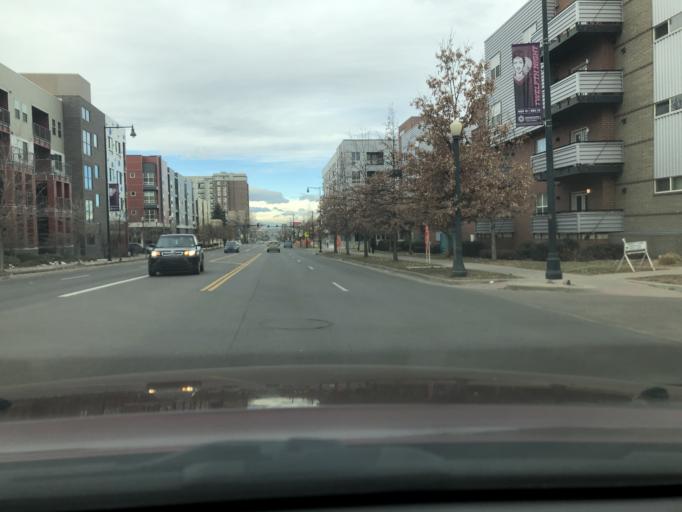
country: US
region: Colorado
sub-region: Denver County
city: Denver
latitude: 39.7485
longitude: -104.9794
